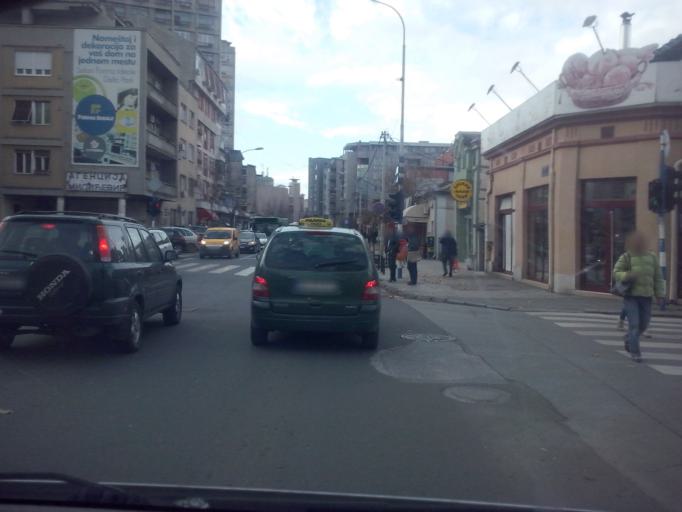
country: RS
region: Central Serbia
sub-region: Sumadijski Okrug
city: Kragujevac
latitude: 44.0136
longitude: 20.9180
